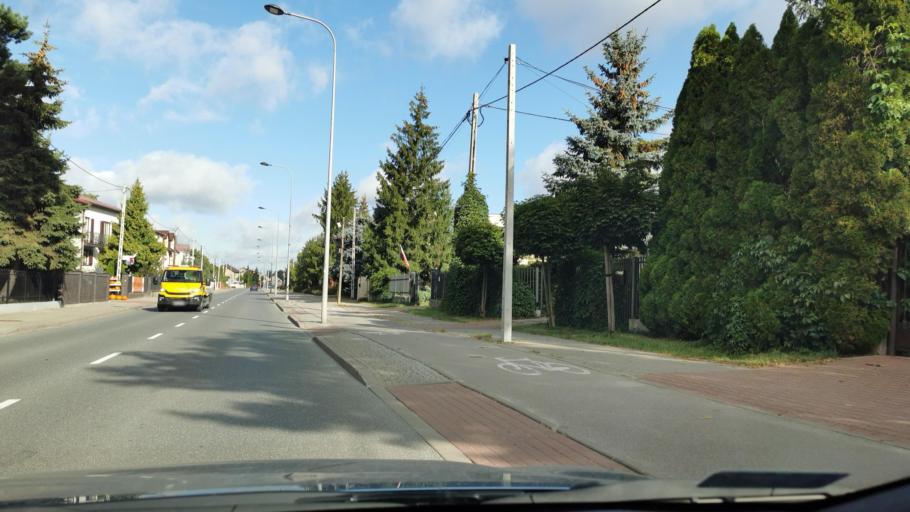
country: PL
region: Masovian Voivodeship
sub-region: Warszawa
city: Kabaty
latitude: 52.1299
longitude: 21.1036
